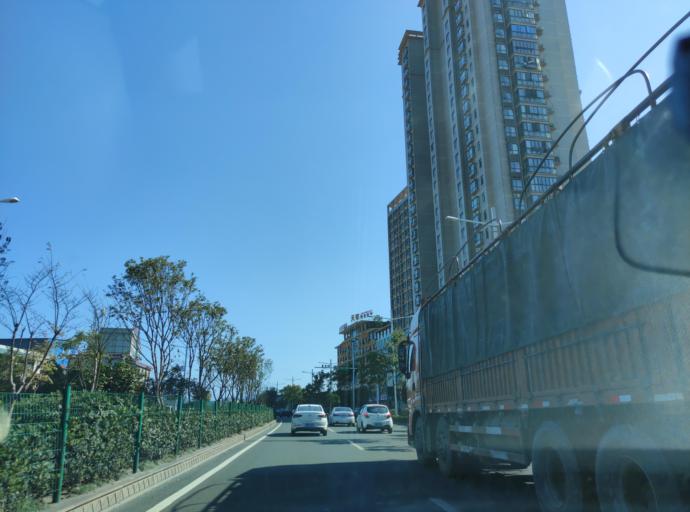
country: CN
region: Jiangxi Sheng
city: Pingxiang
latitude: 27.6588
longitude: 113.8476
